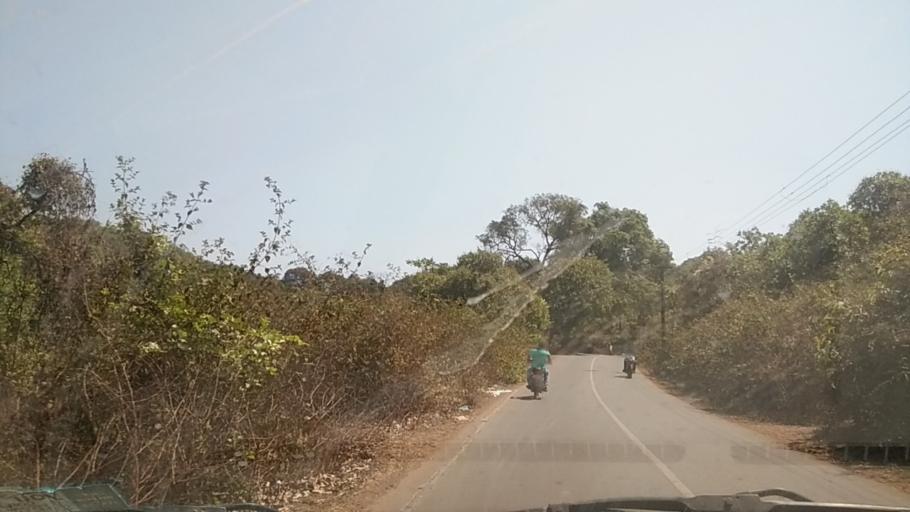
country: IN
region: Goa
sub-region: North Goa
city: Dicholi
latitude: 15.5825
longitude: 73.9336
